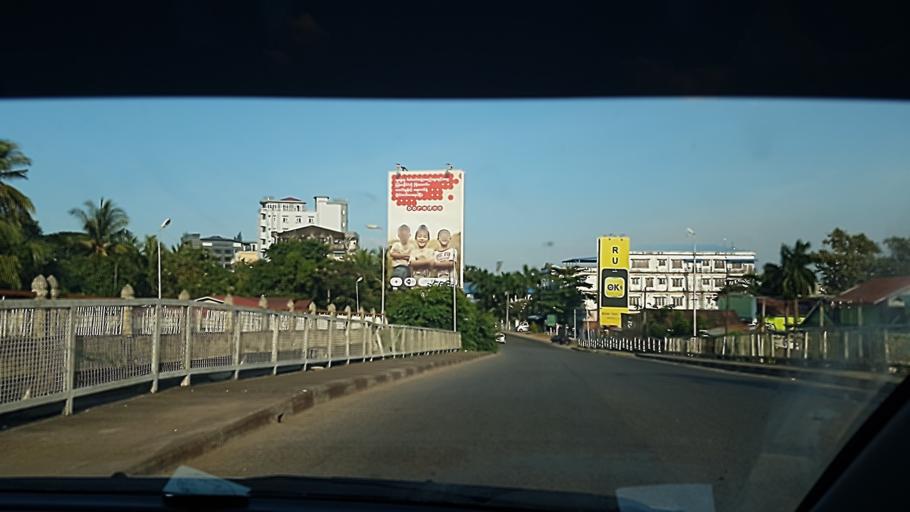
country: MM
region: Yangon
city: Yangon
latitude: 16.8199
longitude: 96.1795
